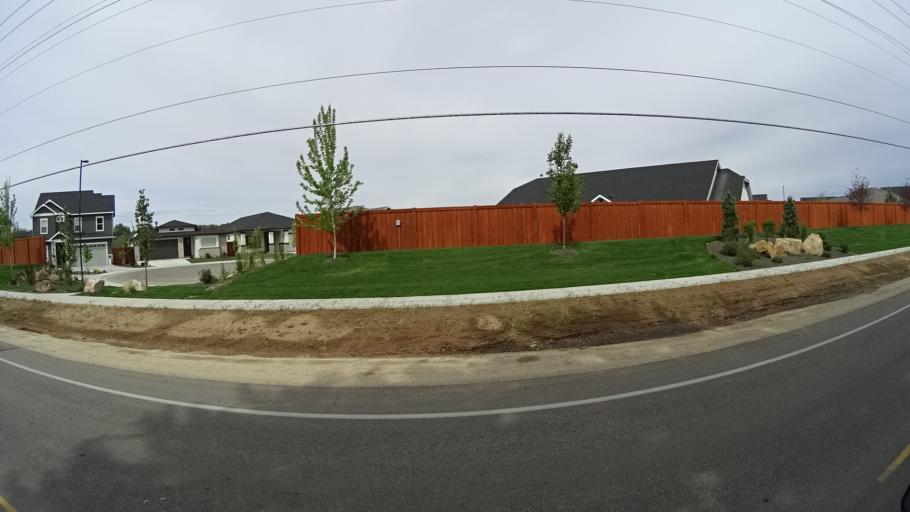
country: US
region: Idaho
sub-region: Ada County
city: Meridian
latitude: 43.5404
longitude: -116.3145
